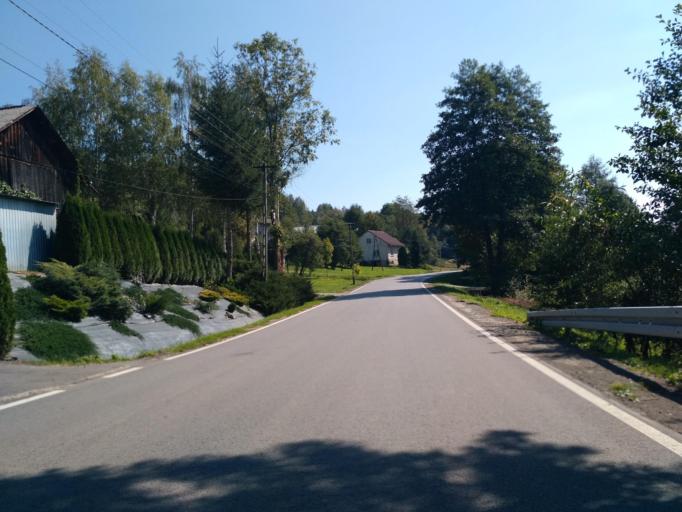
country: PL
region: Subcarpathian Voivodeship
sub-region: Powiat brzozowski
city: Niebocko
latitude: 49.6614
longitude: 22.1291
